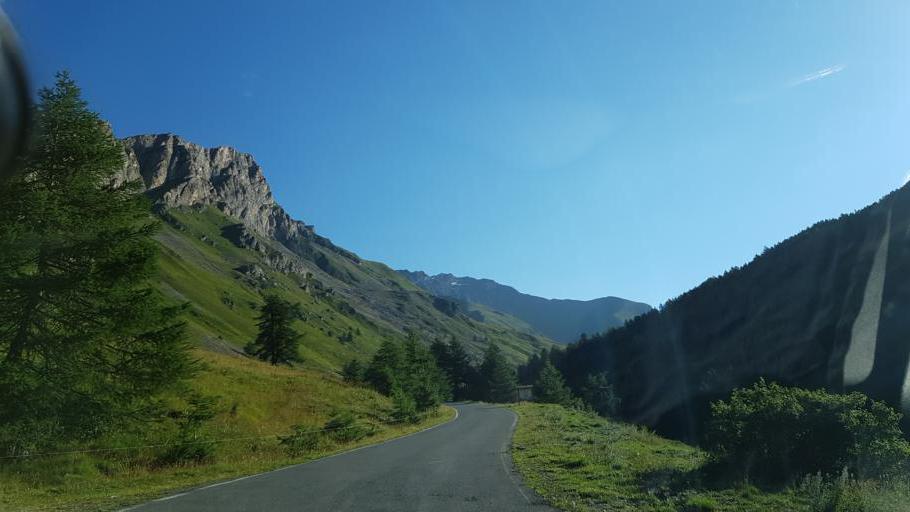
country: IT
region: Piedmont
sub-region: Provincia di Cuneo
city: Pontechianale
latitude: 44.6587
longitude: 6.9900
